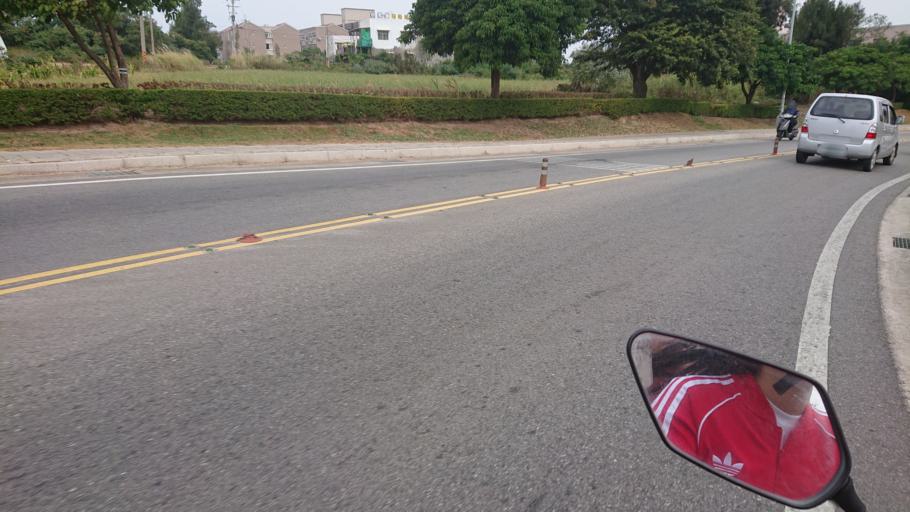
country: TW
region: Fukien
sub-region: Kinmen
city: Jincheng
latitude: 24.4214
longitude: 118.3108
